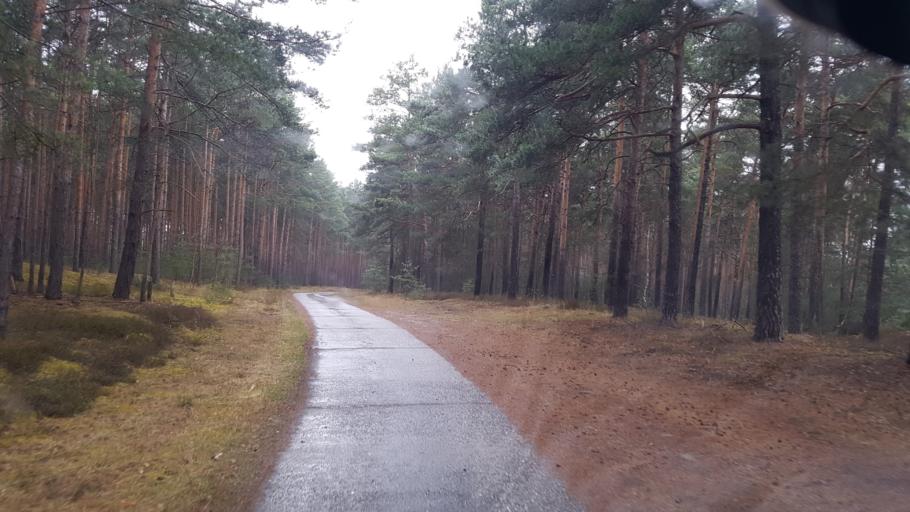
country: DE
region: Brandenburg
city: Grossraschen
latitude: 51.6132
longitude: 13.9838
